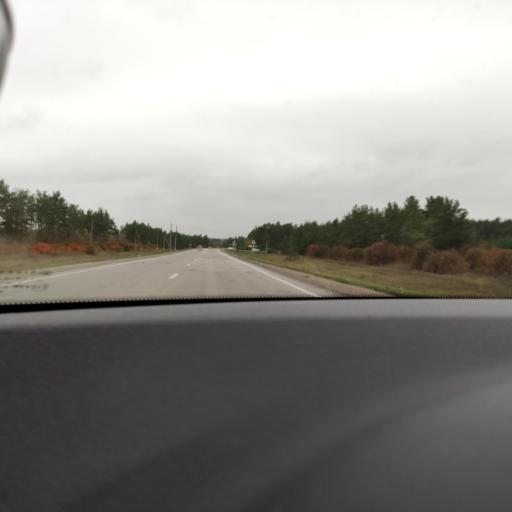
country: RU
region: Samara
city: Mirnyy
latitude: 53.5271
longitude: 50.3112
